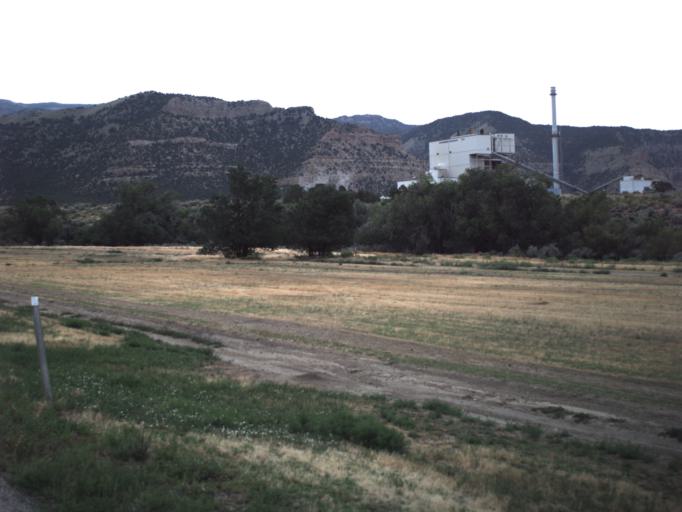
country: US
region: Utah
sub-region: Carbon County
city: East Carbon City
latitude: 39.5495
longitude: -110.3957
